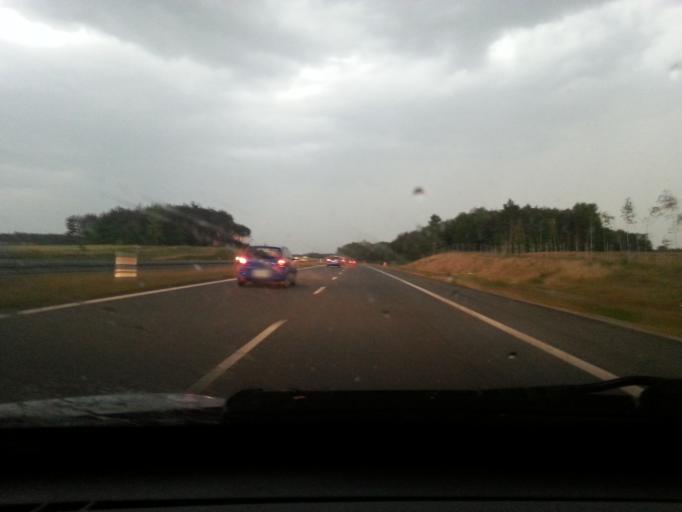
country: PL
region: Lodz Voivodeship
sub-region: powiat Lowicki
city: Lyszkowice
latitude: 51.9651
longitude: 19.8581
